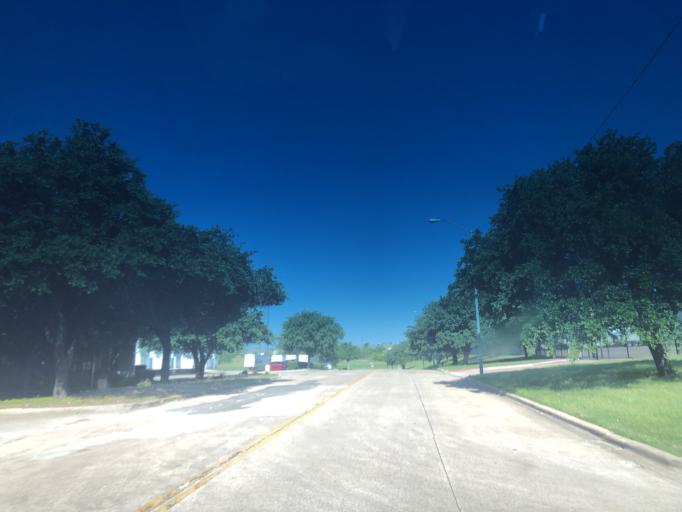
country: US
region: Texas
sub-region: Dallas County
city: Grand Prairie
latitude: 32.7293
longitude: -97.0428
